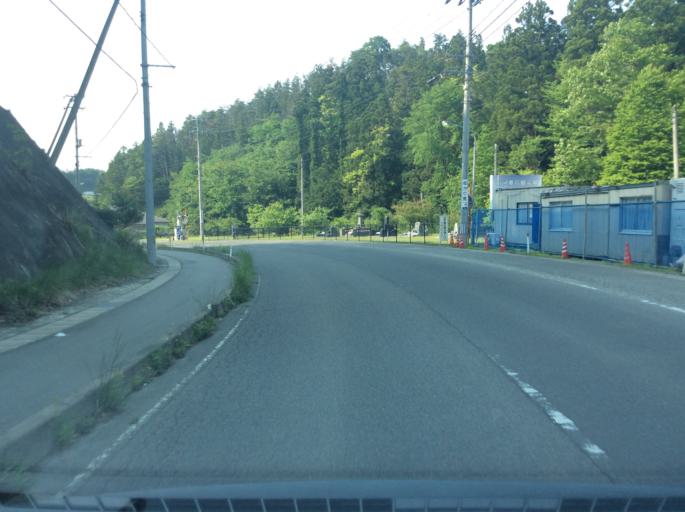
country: JP
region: Fukushima
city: Ishikawa
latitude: 37.1111
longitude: 140.2282
